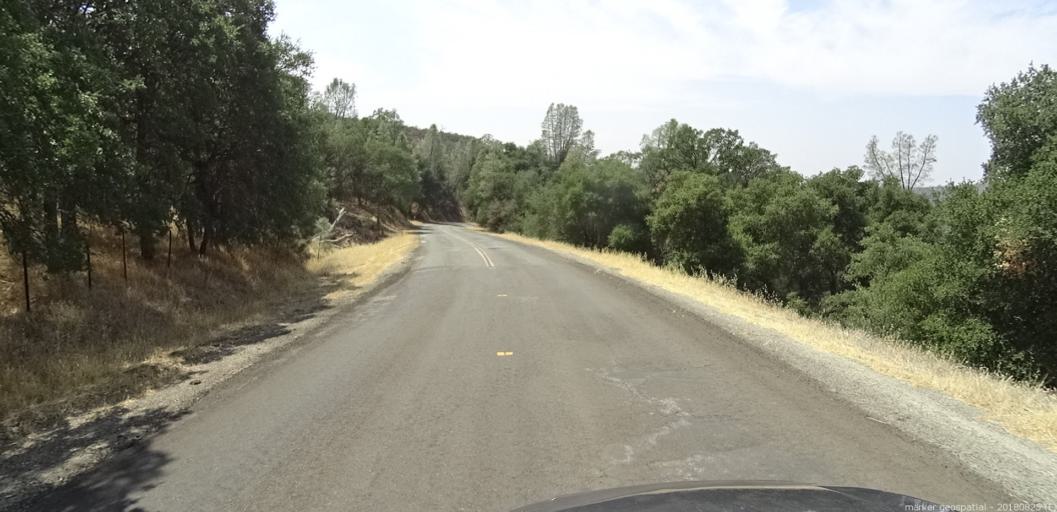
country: US
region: California
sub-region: San Luis Obispo County
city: San Miguel
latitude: 35.9101
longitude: -120.5444
